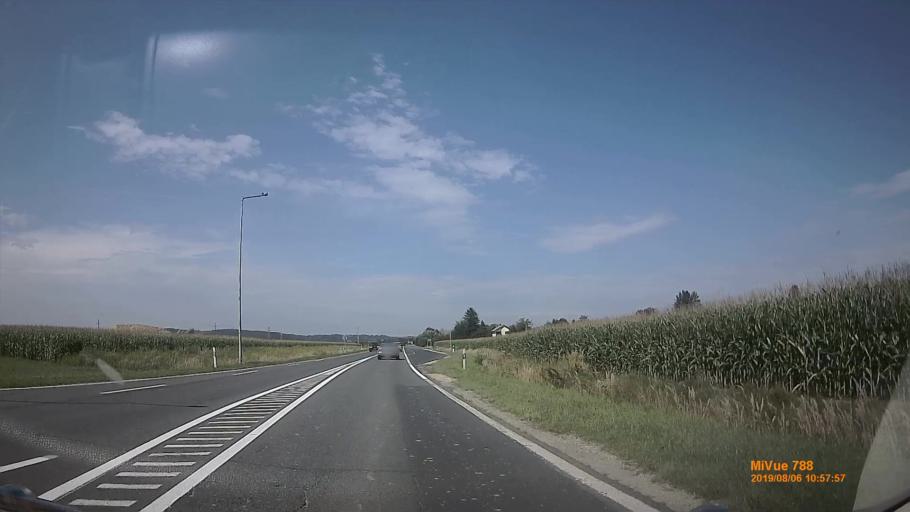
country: HU
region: Vas
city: Szentgotthard
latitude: 46.9782
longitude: 16.2940
